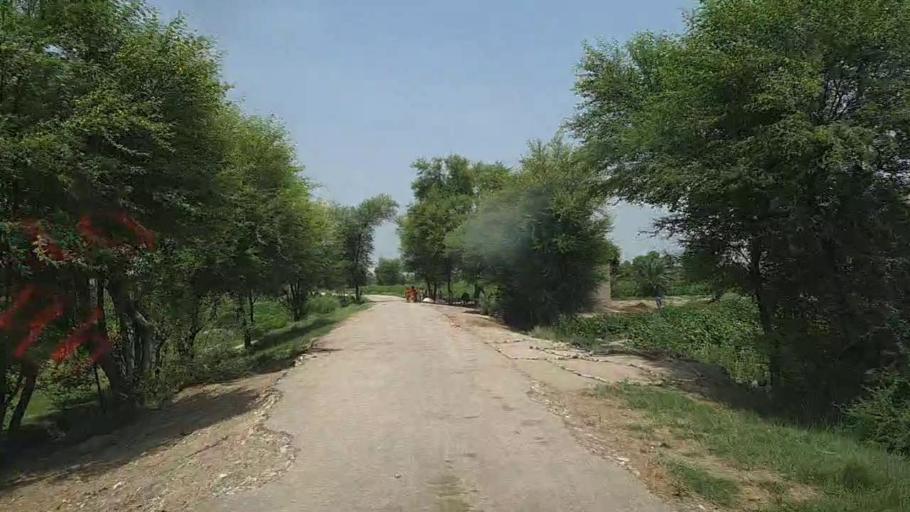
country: PK
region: Sindh
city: Pano Aqil
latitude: 27.8272
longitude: 69.2127
